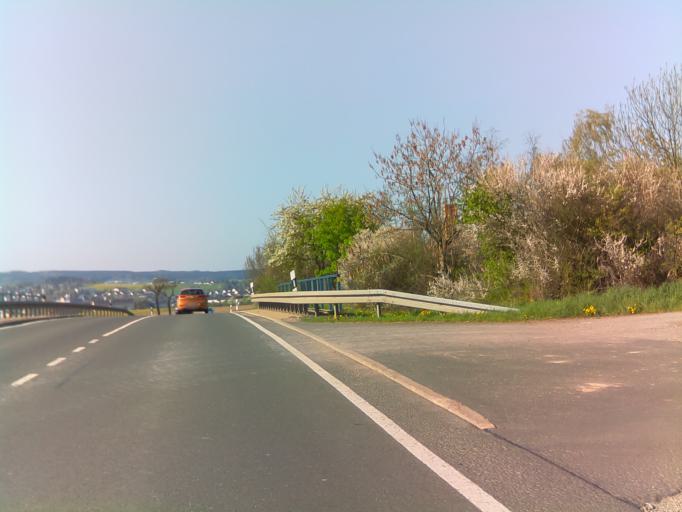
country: DE
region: Thuringia
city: Oettersdorf
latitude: 50.5966
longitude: 11.8223
